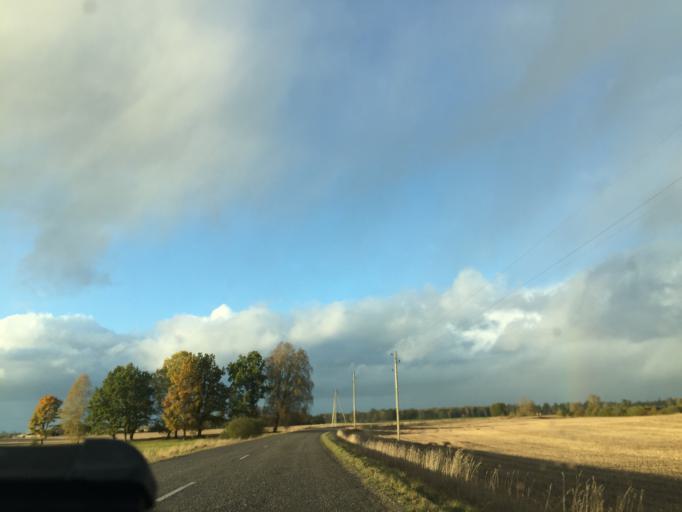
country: LV
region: Broceni
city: Broceni
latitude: 56.8739
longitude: 22.3801
